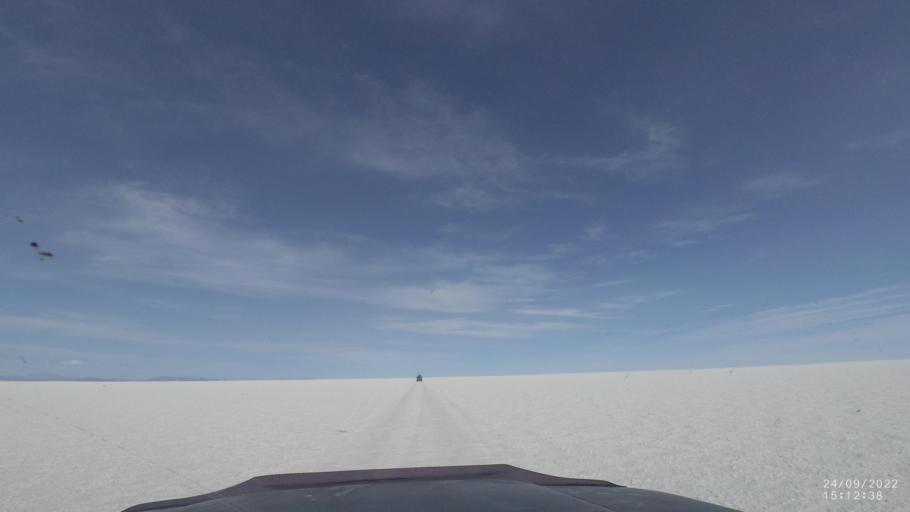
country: BO
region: Potosi
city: Colchani
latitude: -19.9515
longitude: -67.4698
